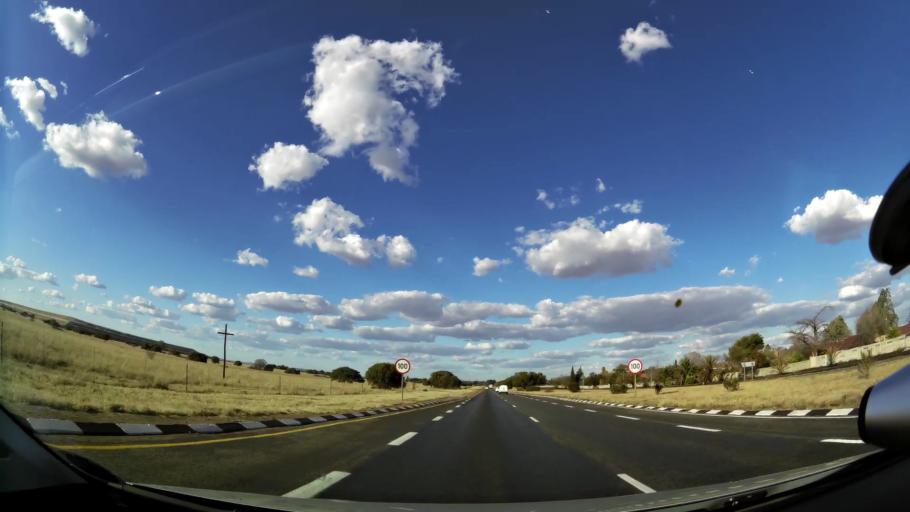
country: ZA
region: North-West
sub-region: Dr Kenneth Kaunda District Municipality
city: Stilfontein
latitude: -26.8403
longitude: 26.7593
